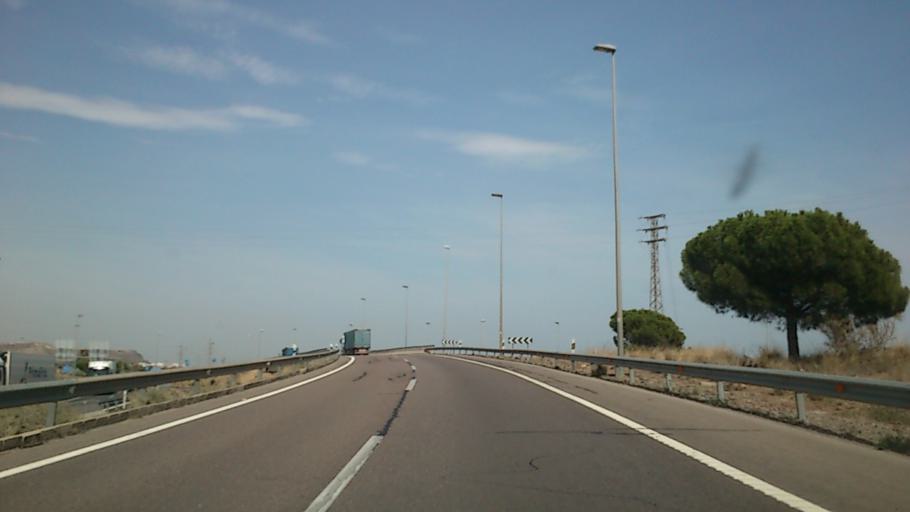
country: ES
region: Valencia
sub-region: Provincia de Valencia
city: Pucol
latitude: 39.6327
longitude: -0.3052
